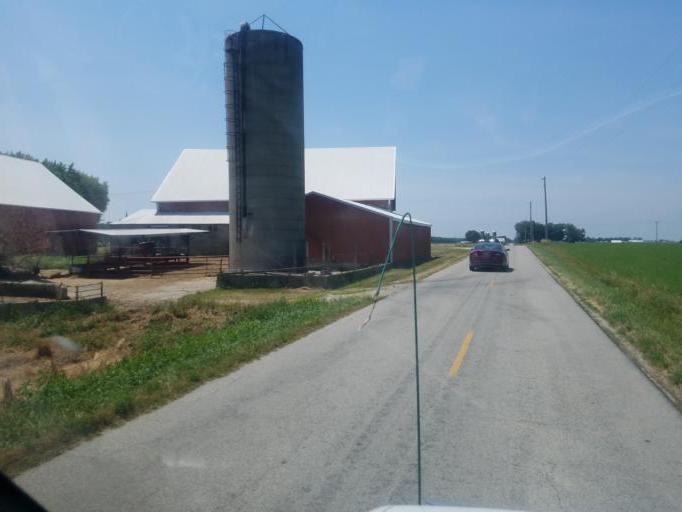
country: US
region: Ohio
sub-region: Shelby County
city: Fort Loramie
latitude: 40.3291
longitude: -84.3444
